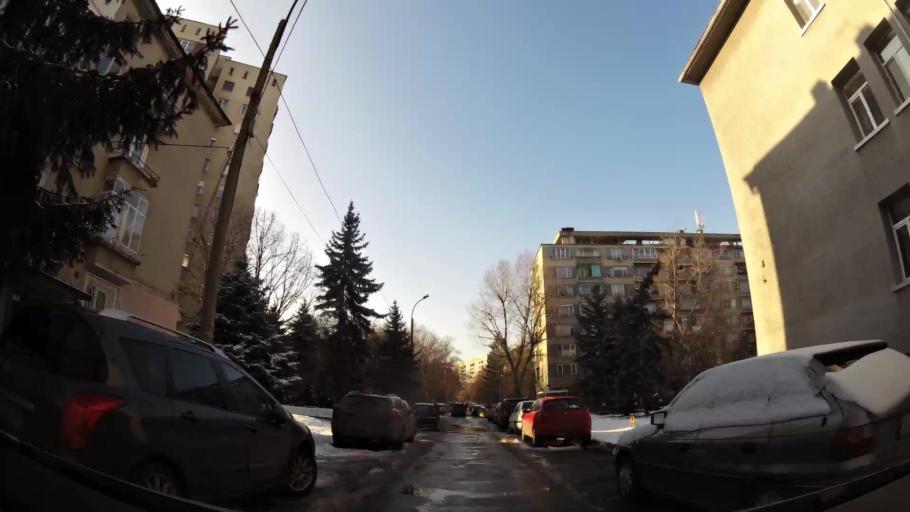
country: BG
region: Sofia-Capital
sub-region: Stolichna Obshtina
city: Sofia
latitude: 42.6768
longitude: 23.3647
